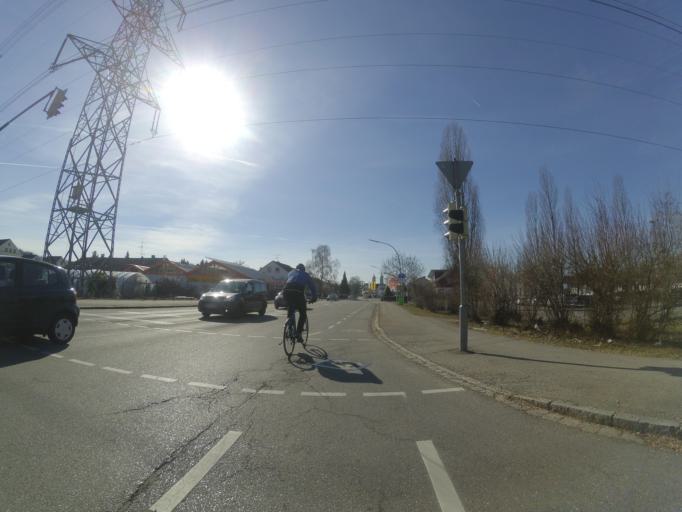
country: DE
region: Baden-Wuerttemberg
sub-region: Tuebingen Region
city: Ravensburg
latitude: 47.7678
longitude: 9.6029
